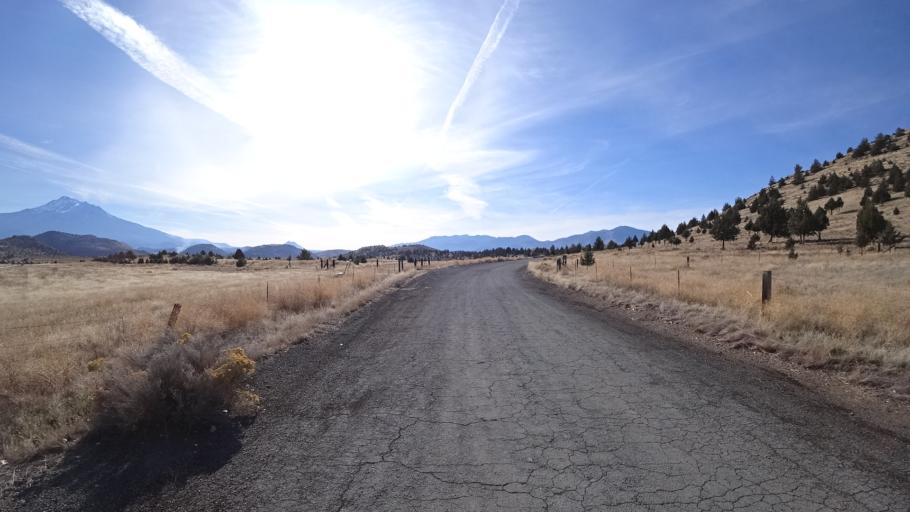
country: US
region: California
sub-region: Siskiyou County
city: Weed
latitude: 41.5590
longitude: -122.4711
